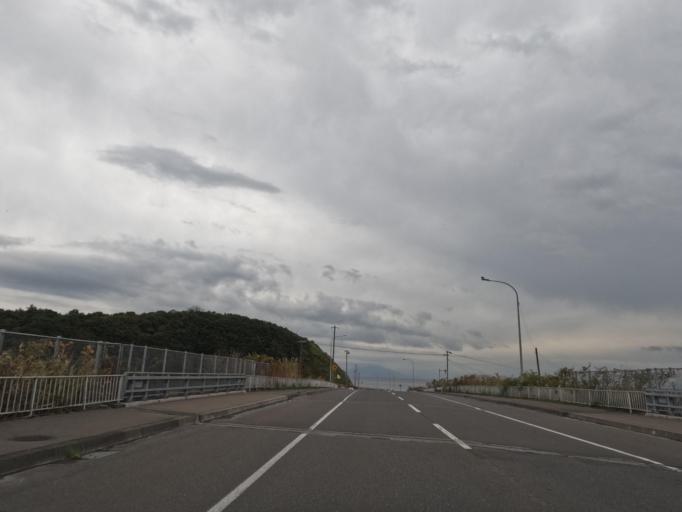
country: JP
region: Hokkaido
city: Date
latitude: 42.3812
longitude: 140.9103
